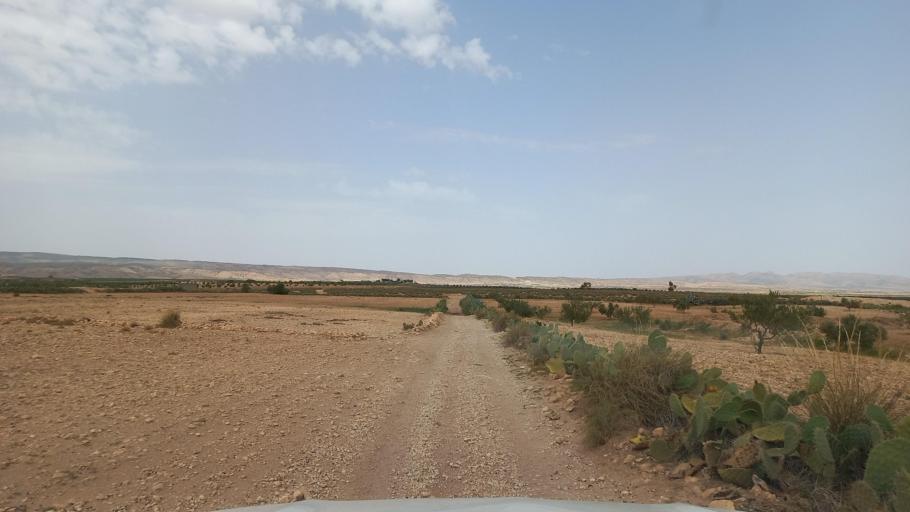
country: TN
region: Al Qasrayn
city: Kasserine
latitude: 35.2907
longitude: 9.0056
